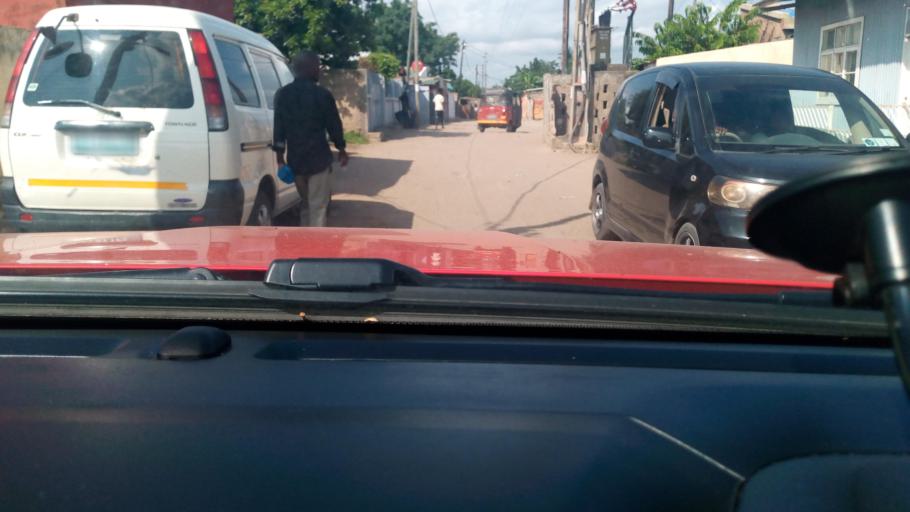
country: MZ
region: Maputo City
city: Maputo
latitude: -25.9159
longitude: 32.5629
